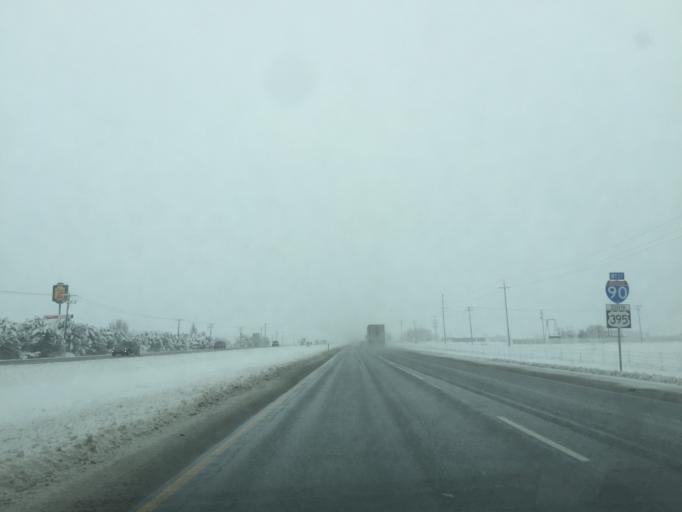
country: US
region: Washington
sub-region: Spokane County
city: Airway Heights
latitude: 47.5884
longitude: -117.5693
